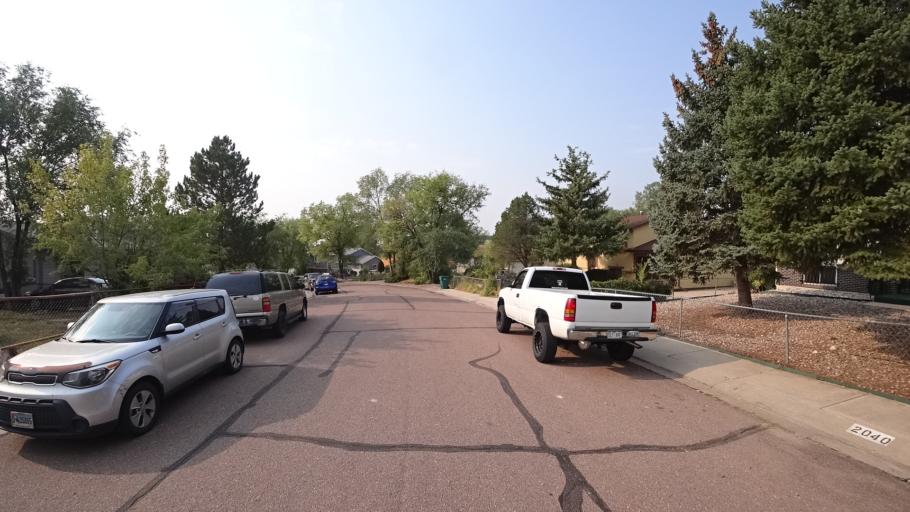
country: US
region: Colorado
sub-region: El Paso County
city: Stratmoor
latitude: 38.8024
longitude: -104.7638
